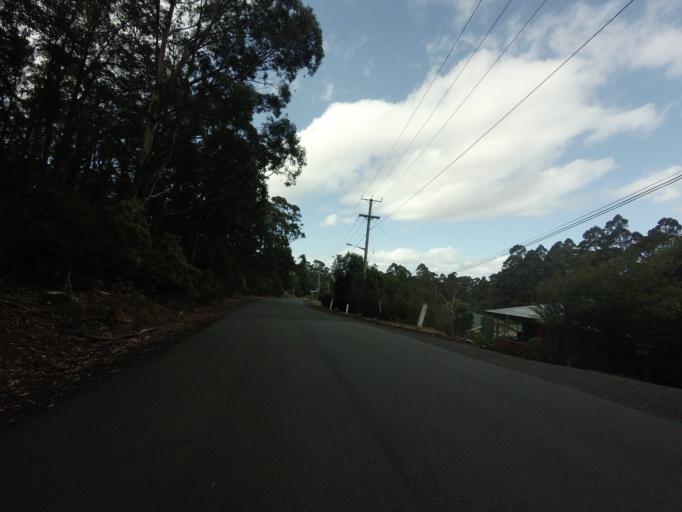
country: AU
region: Tasmania
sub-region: Hobart
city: Dynnyrne
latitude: -42.9063
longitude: 147.2674
